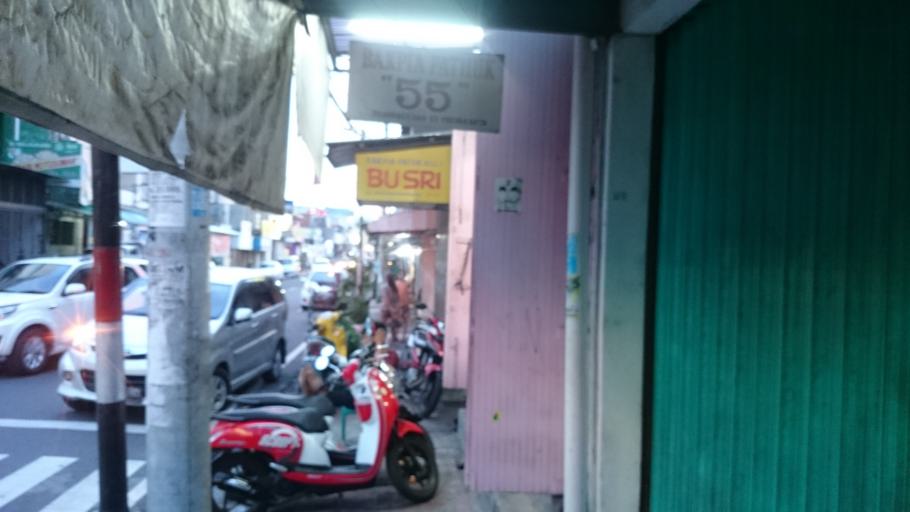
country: ID
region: Daerah Istimewa Yogyakarta
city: Yogyakarta
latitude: -7.7968
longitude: 110.3621
